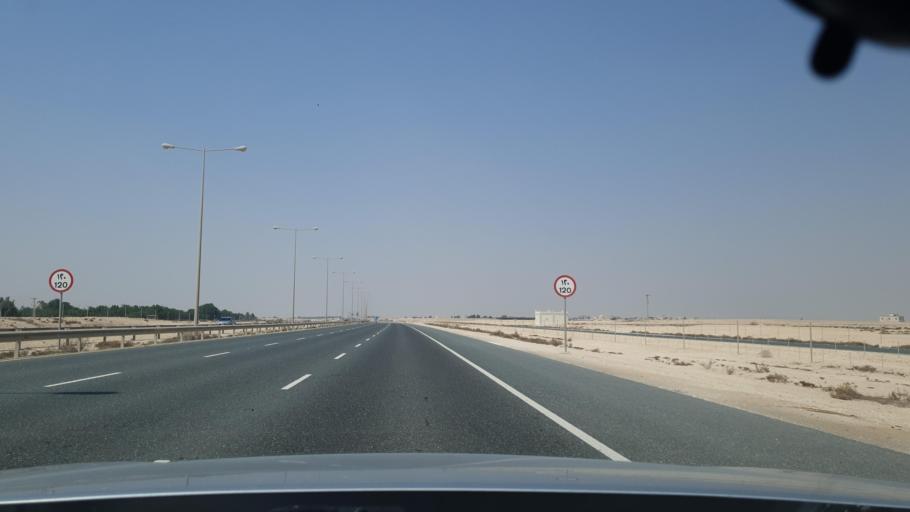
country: QA
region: Al Khawr
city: Al Khawr
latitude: 25.7743
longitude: 51.4106
